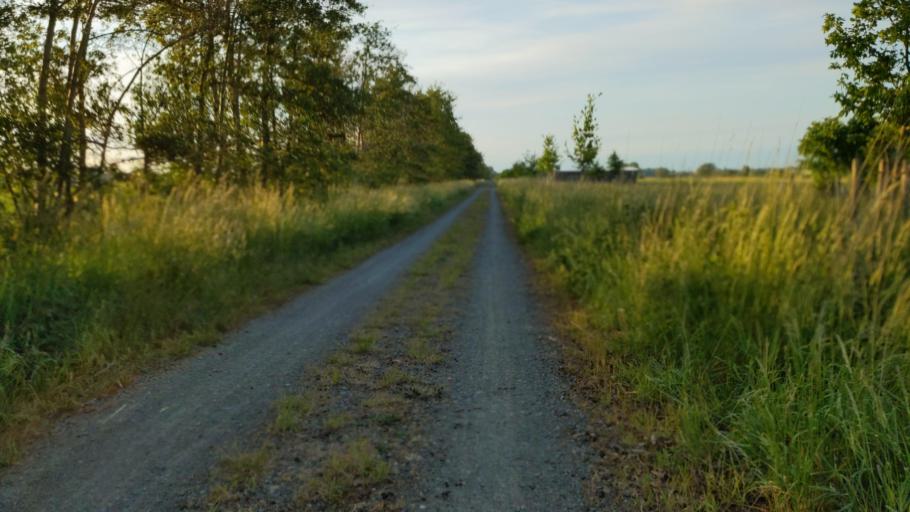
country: DE
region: Lower Saxony
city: Sickte
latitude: 52.2264
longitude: 10.5955
